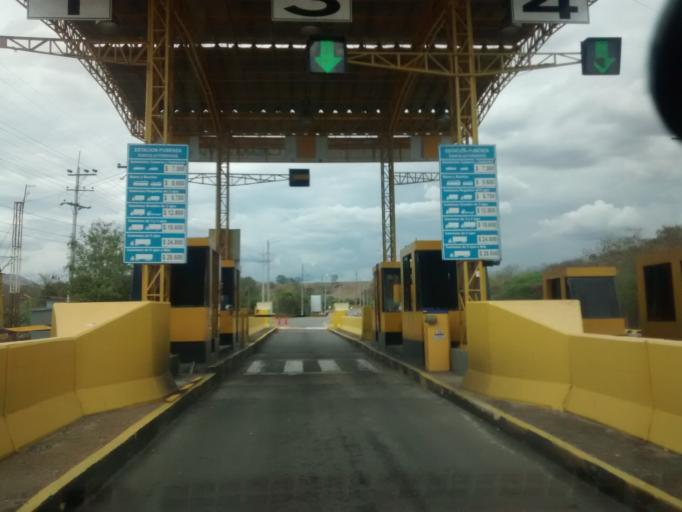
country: CO
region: Cundinamarca
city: Agua de Dios
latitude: 4.4033
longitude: -74.7316
